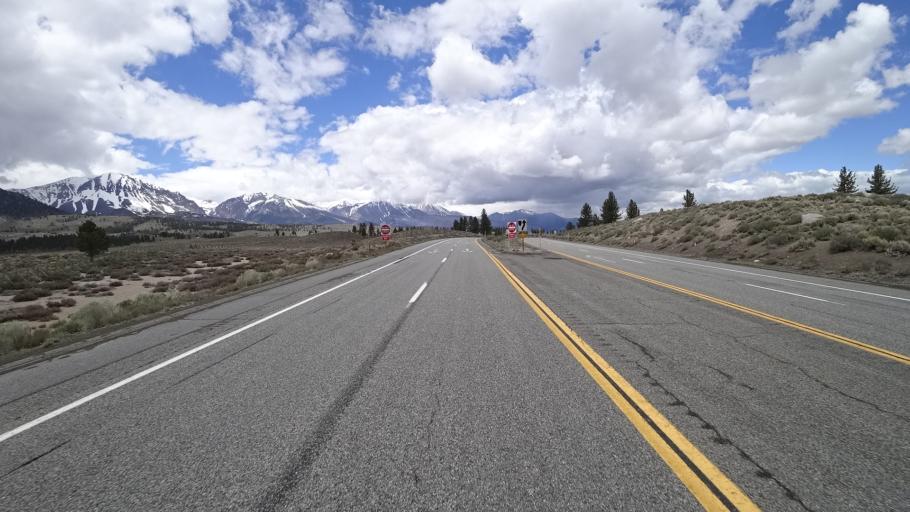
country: US
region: California
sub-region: Mono County
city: Mammoth Lakes
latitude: 37.8163
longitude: -119.0582
